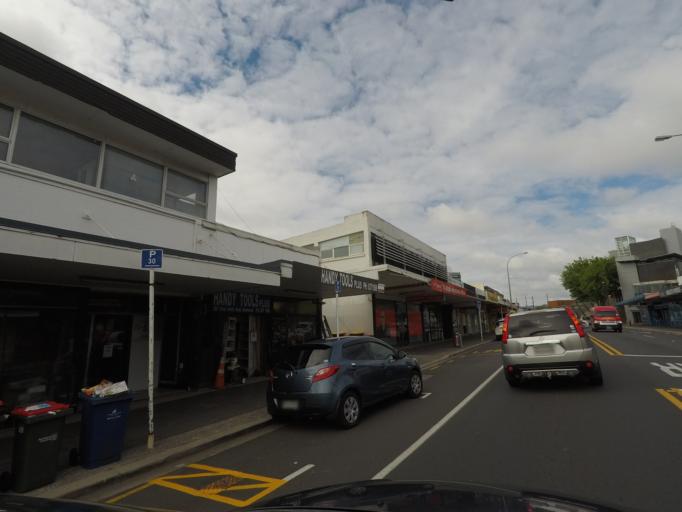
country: NZ
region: Auckland
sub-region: Auckland
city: Rosebank
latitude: -36.8797
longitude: 174.6318
